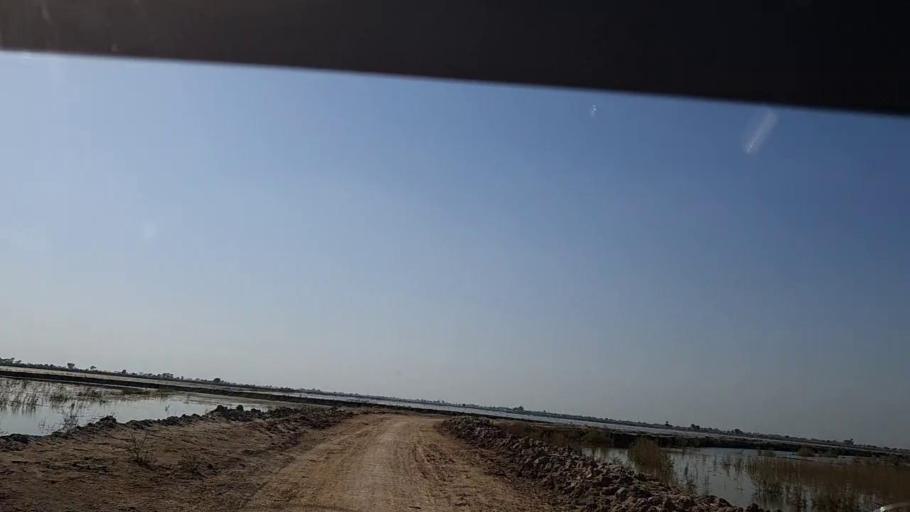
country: PK
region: Sindh
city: Tangwani
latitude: 28.3539
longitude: 69.0397
